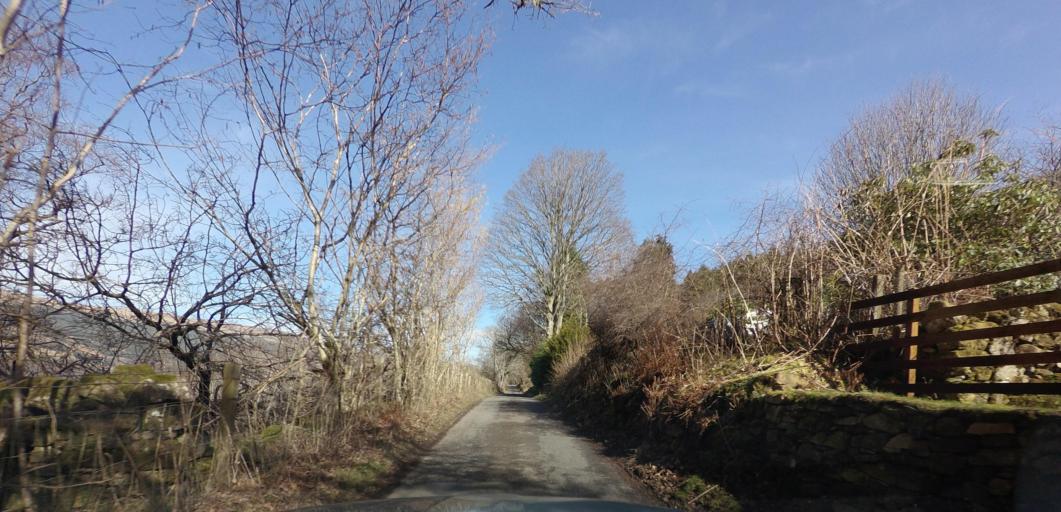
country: GB
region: Scotland
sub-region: Perth and Kinross
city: Comrie
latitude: 56.5452
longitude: -4.0986
